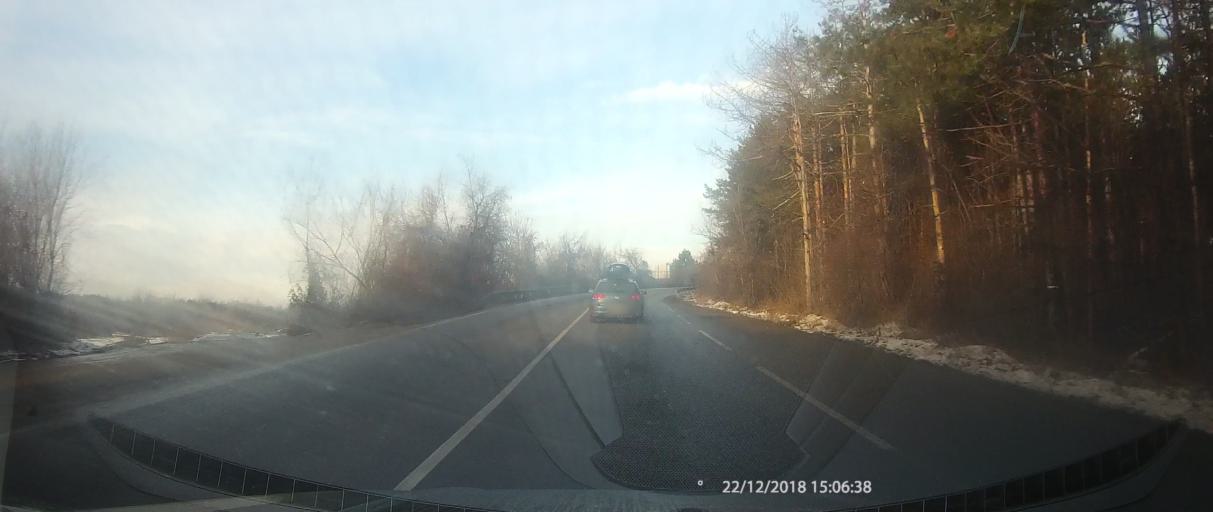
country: BG
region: Ruse
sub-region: Obshtina Borovo
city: Borovo
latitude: 43.4807
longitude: 25.7691
